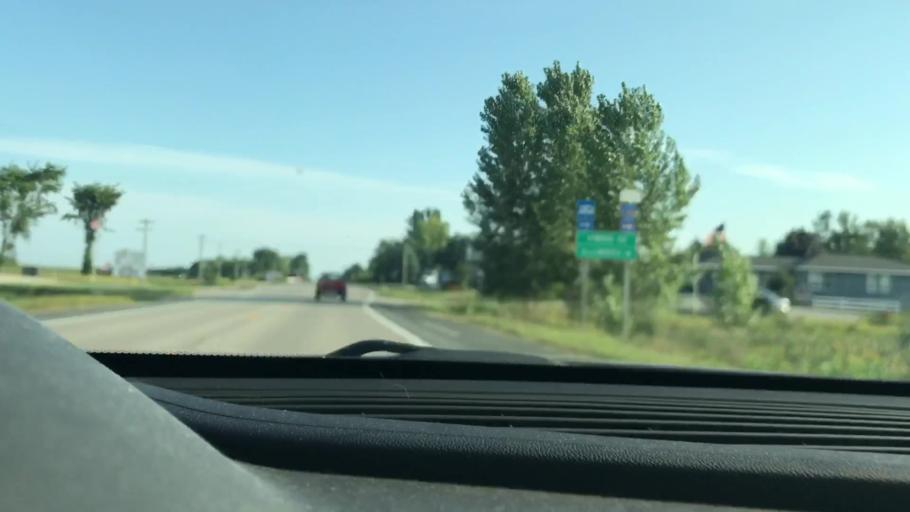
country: US
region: Michigan
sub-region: Charlevoix County
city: Charlevoix
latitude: 45.1845
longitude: -85.3451
